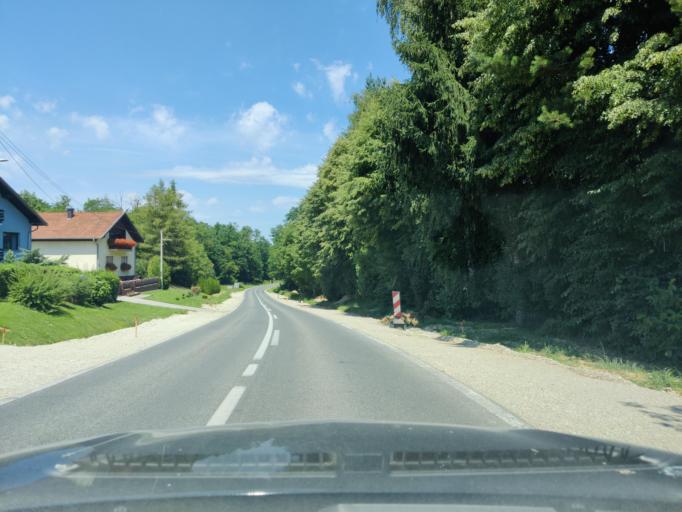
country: HR
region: Medimurska
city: Mackovec
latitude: 46.4523
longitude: 16.4320
